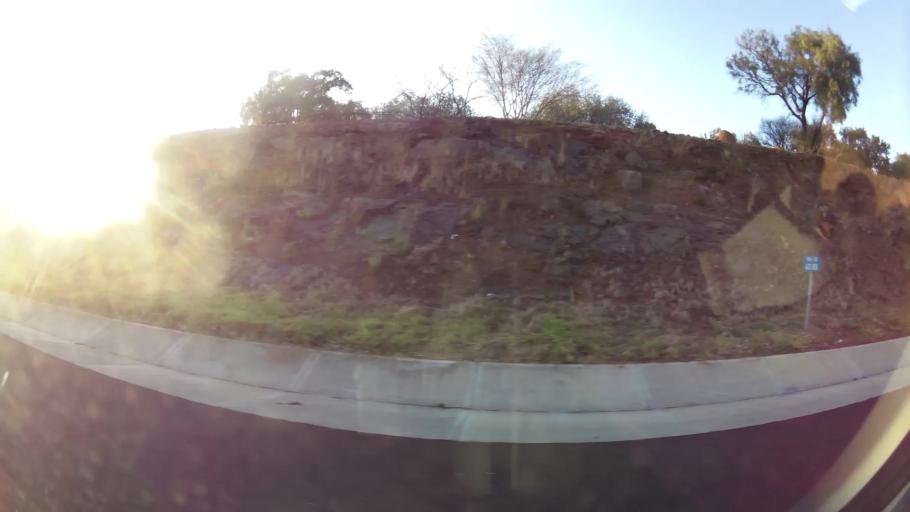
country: ZA
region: Orange Free State
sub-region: Mangaung Metropolitan Municipality
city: Bloemfontein
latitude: -29.0989
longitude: 26.1658
